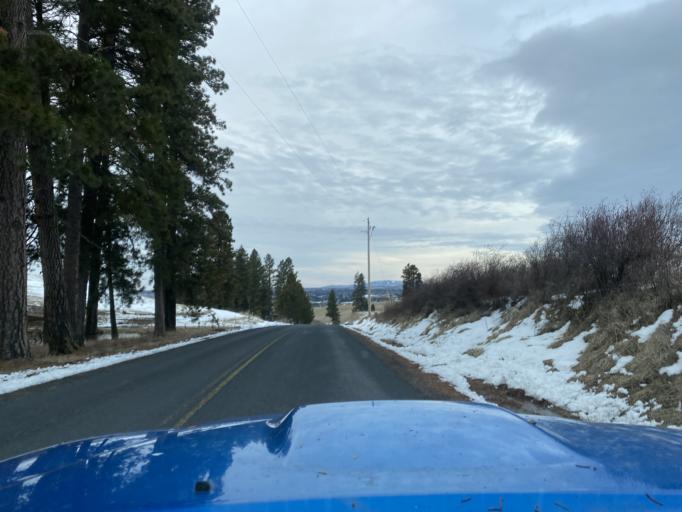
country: US
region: Idaho
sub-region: Latah County
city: Moscow
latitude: 46.7008
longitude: -116.9327
